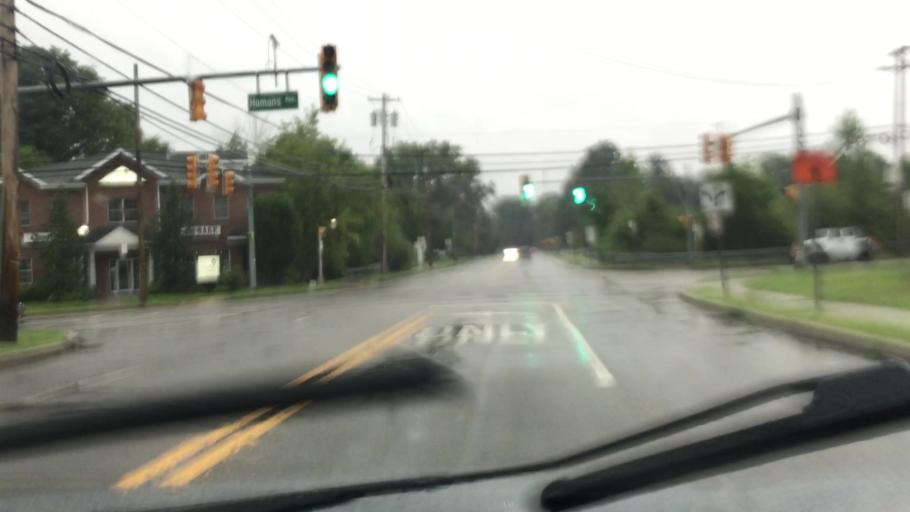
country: US
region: New Jersey
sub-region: Bergen County
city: Closter
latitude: 40.9687
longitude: -73.9525
